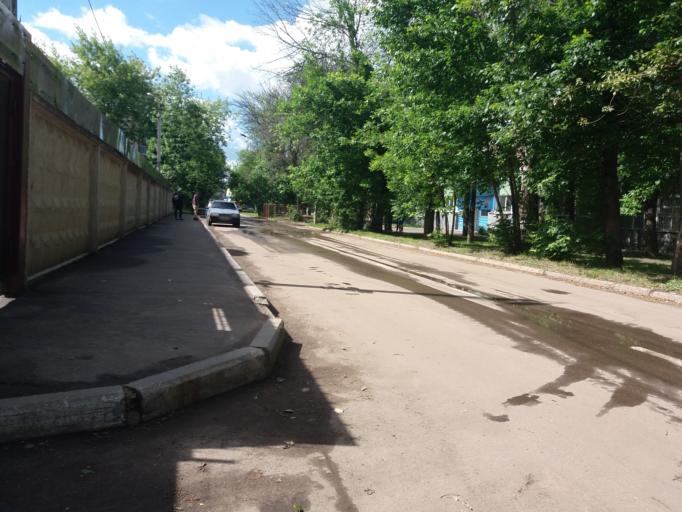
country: RU
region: Jaroslavl
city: Yaroslavl
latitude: 57.6410
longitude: 39.8508
